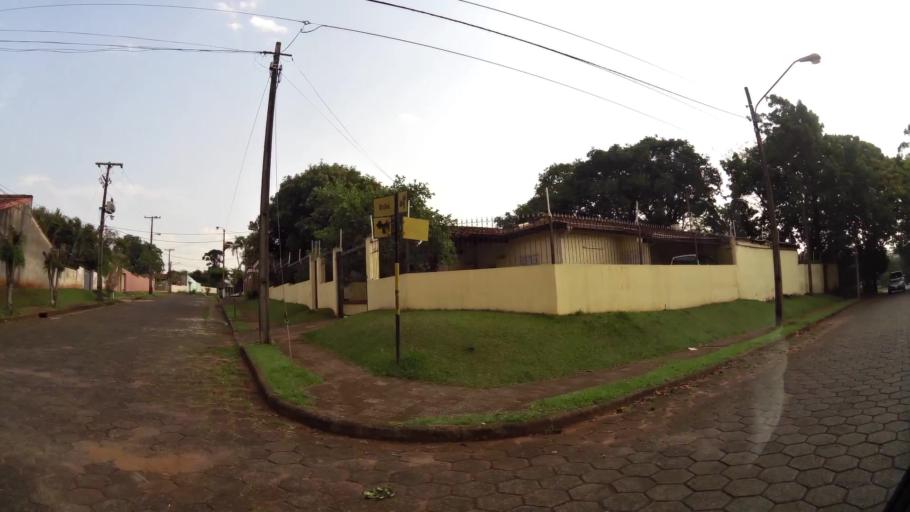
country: PY
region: Alto Parana
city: Presidente Franco
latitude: -25.5248
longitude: -54.6329
